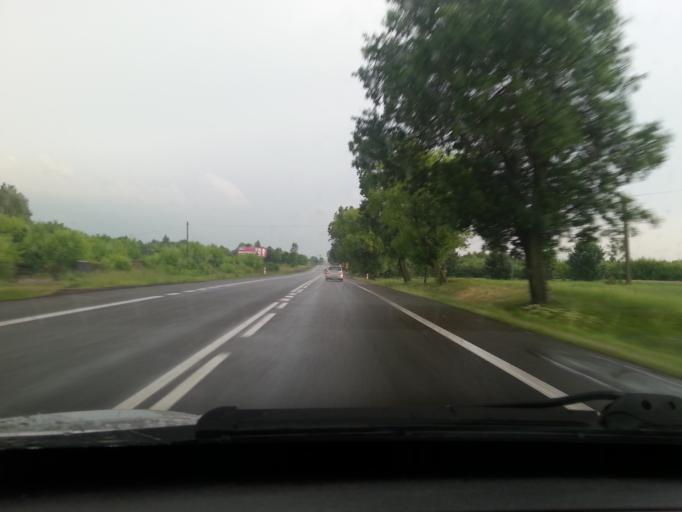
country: PL
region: Lodz Voivodeship
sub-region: Powiat zgierski
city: Strykow
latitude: 51.8601
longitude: 19.5660
